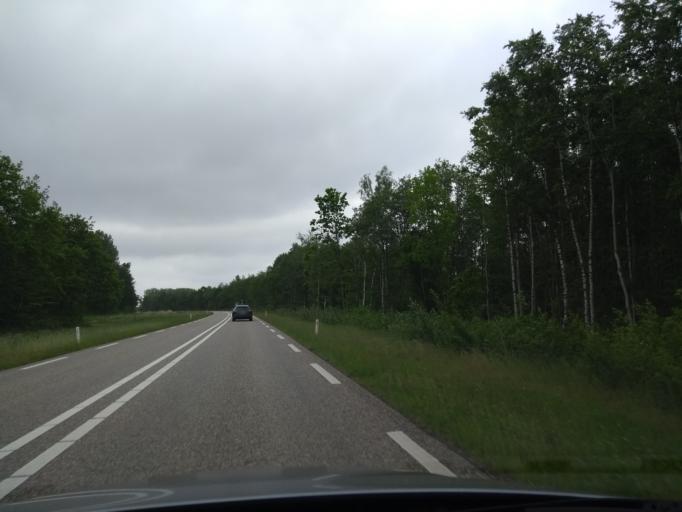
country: NL
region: Friesland
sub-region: Gemeente Dongeradeel
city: Anjum
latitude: 53.4024
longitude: 6.2308
